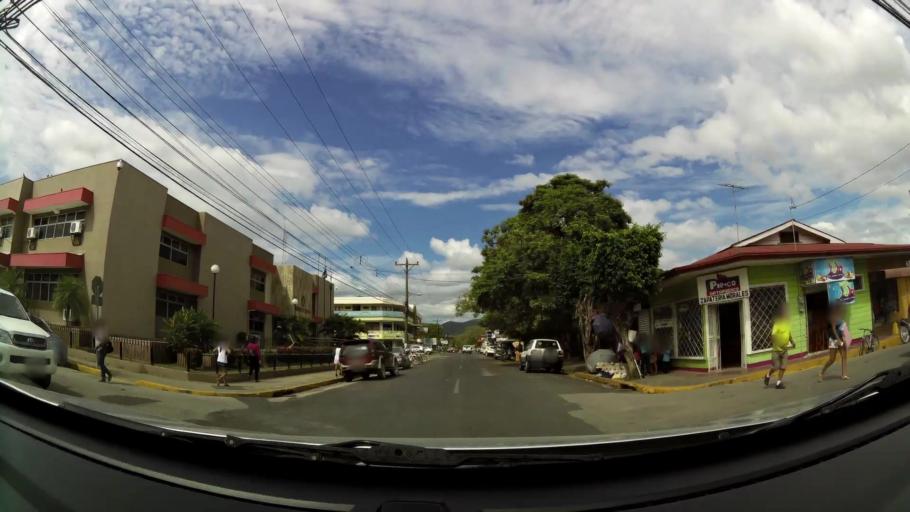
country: CR
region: Guanacaste
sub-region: Canton de Nicoya
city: Nicoya
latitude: 10.1453
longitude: -85.4524
